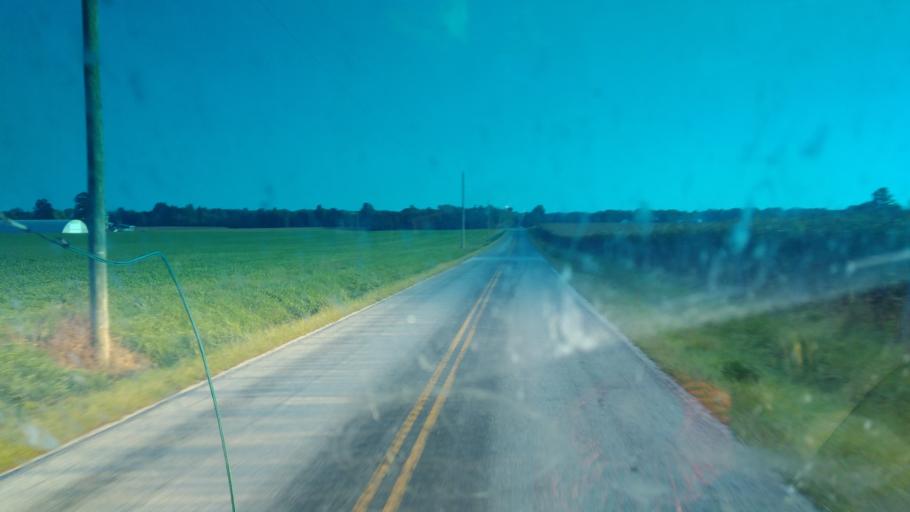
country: US
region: Ohio
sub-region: Crawford County
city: Bucyrus
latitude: 40.8481
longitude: -82.8730
